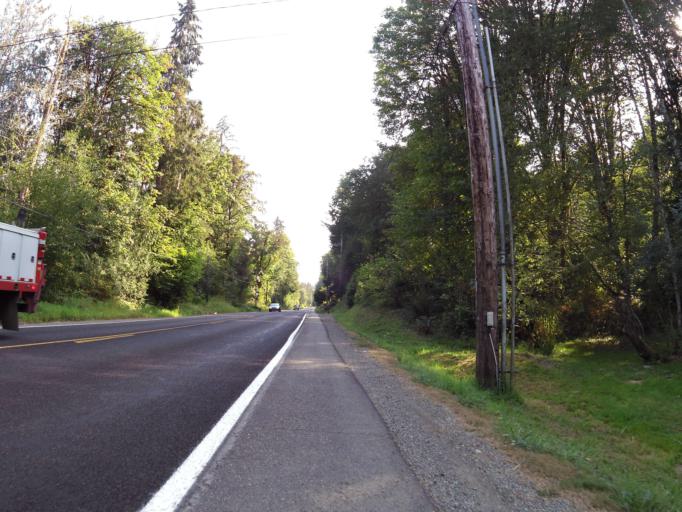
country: US
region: Washington
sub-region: Mason County
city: Belfair
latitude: 47.5093
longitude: -122.7955
